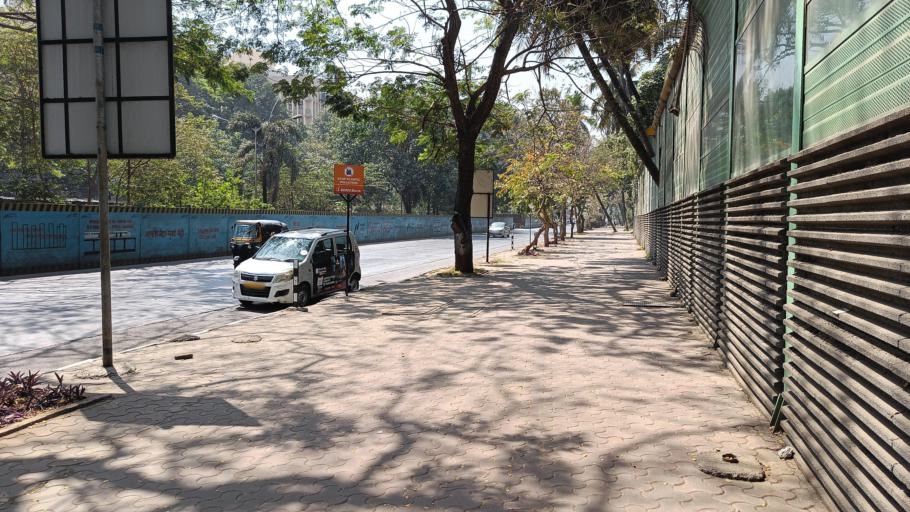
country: IN
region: Maharashtra
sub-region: Mumbai Suburban
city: Mumbai
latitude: 19.0573
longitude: 72.8523
